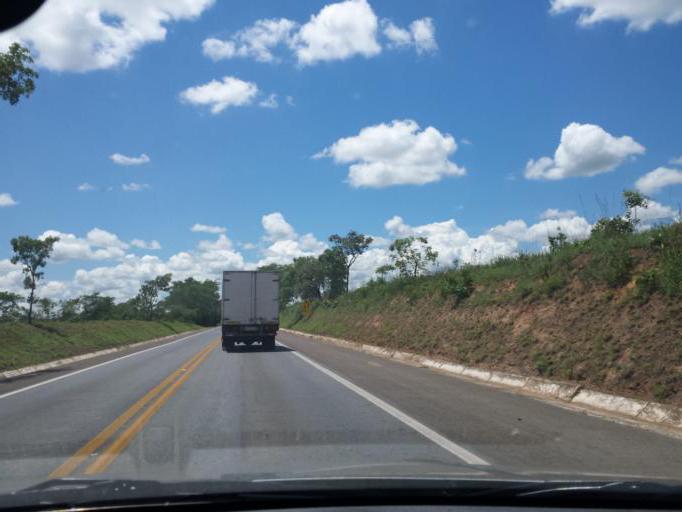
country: BR
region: Goias
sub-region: Cristalina
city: Cristalina
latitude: -16.5979
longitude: -47.7744
